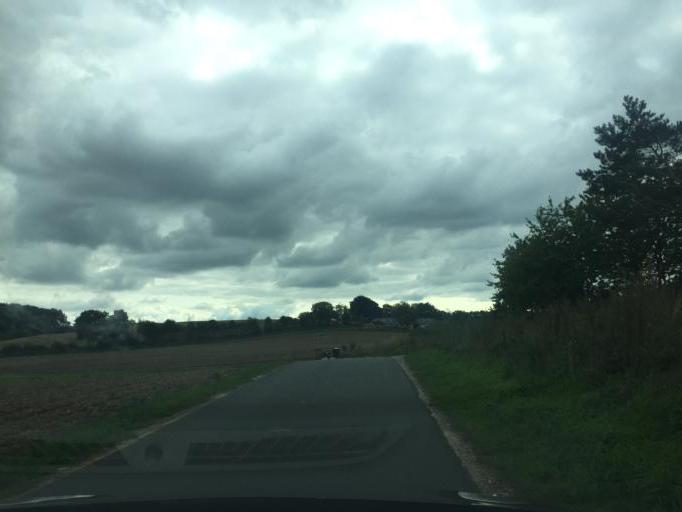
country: DK
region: South Denmark
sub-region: Assens Kommune
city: Tommerup Stationsby
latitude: 55.3635
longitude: 10.2169
